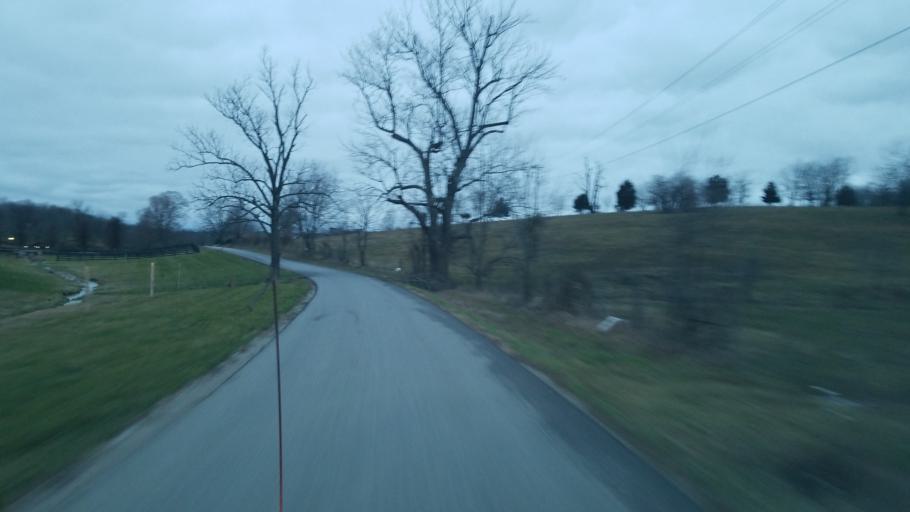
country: US
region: Kentucky
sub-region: Fleming County
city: Flemingsburg
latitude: 38.5057
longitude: -83.6865
